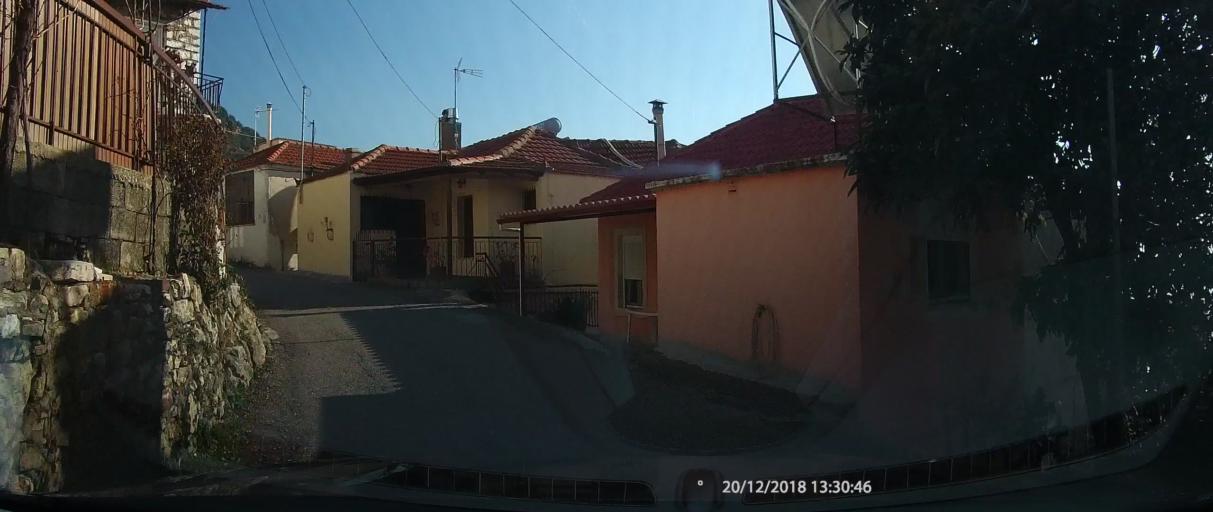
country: GR
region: West Greece
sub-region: Nomos Aitolias kai Akarnanias
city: Paravola
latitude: 38.6325
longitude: 21.5841
